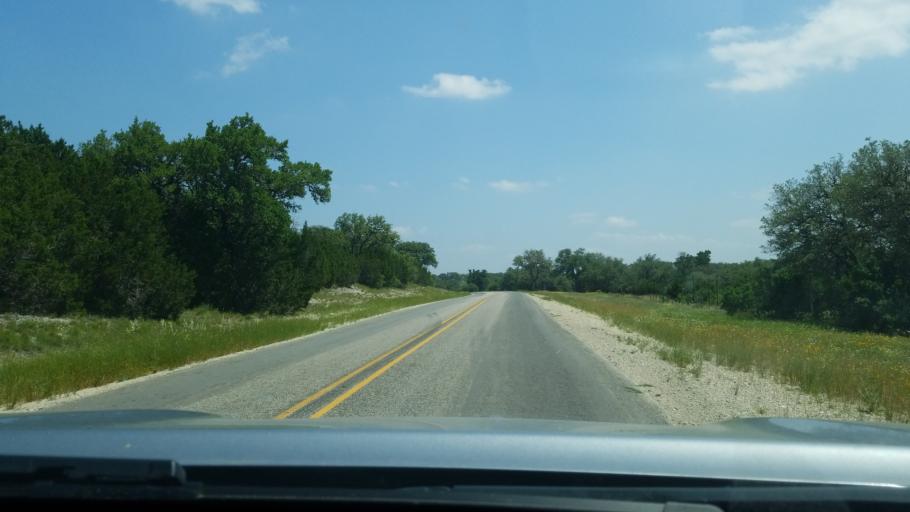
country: US
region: Texas
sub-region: Blanco County
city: Blanco
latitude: 29.9811
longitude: -98.5487
